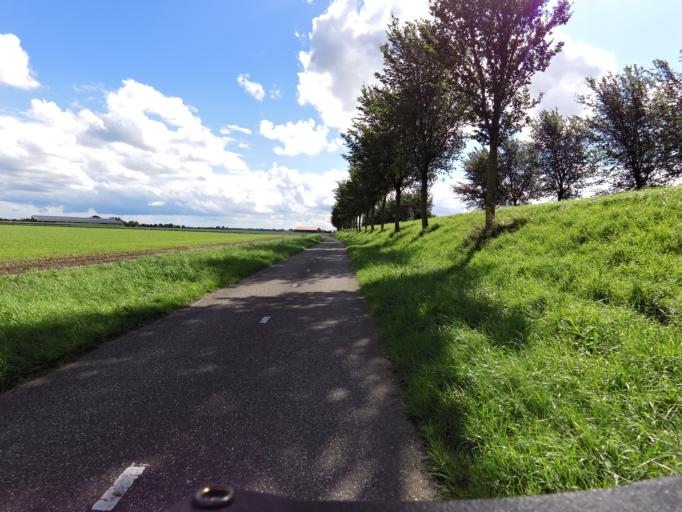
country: NL
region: South Holland
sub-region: Gemeente Goeree-Overflakkee
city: Middelharnis
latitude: 51.7093
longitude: 4.2630
